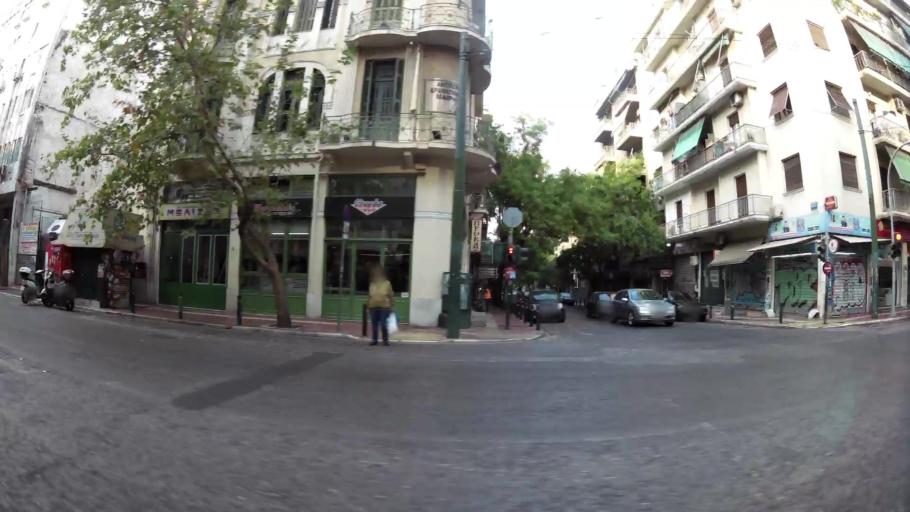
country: GR
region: Attica
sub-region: Nomarchia Athinas
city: Athens
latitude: 37.9905
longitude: 23.7267
